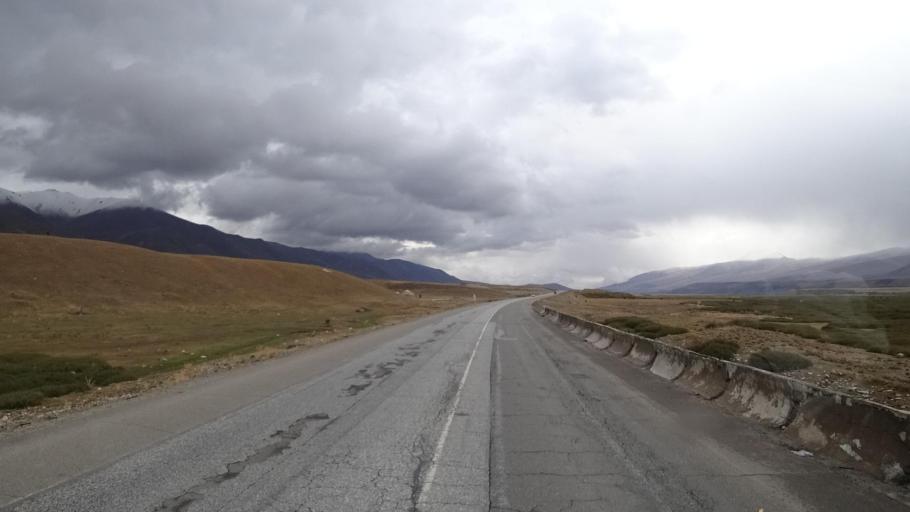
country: KG
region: Jalal-Abad
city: Uch-Terek
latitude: 42.1903
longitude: 73.4200
